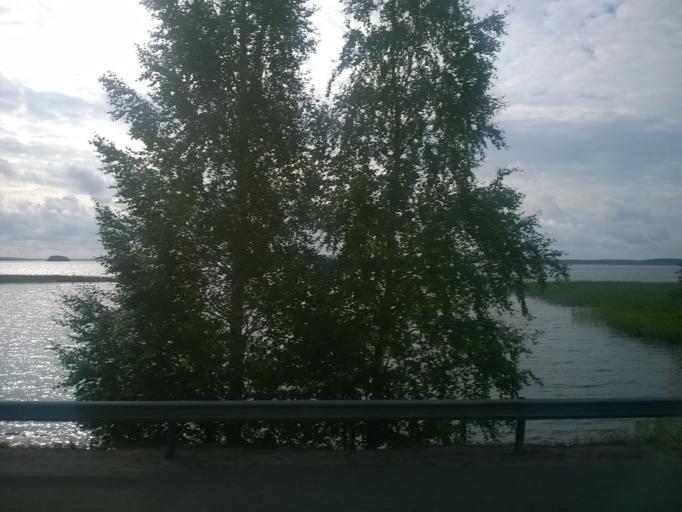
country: FI
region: Kainuu
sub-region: Kajaani
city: Sotkamo
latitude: 64.1294
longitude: 28.3736
